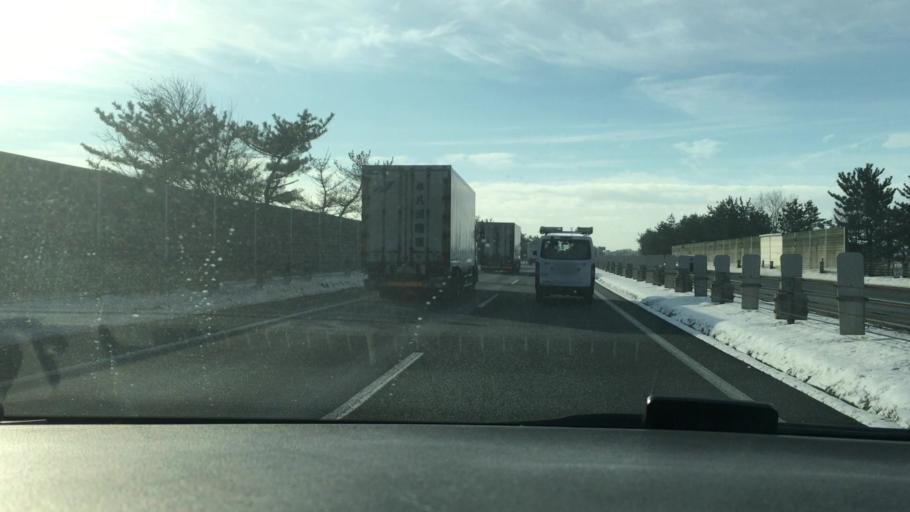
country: JP
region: Iwate
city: Hanamaki
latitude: 39.3969
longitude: 141.0926
